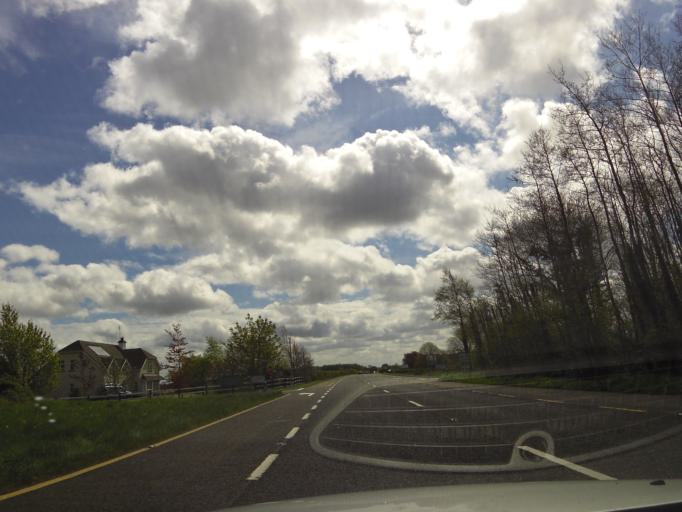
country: IE
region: Connaught
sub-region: Maigh Eo
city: Claremorris
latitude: 53.6972
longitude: -8.9765
